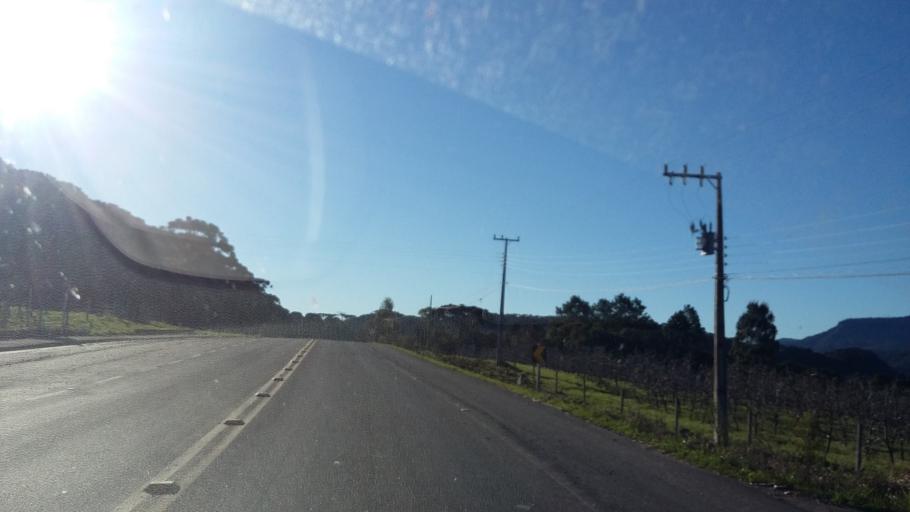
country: BR
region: Santa Catarina
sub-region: Lauro Muller
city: Lauro Muller
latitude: -28.0127
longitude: -49.5318
